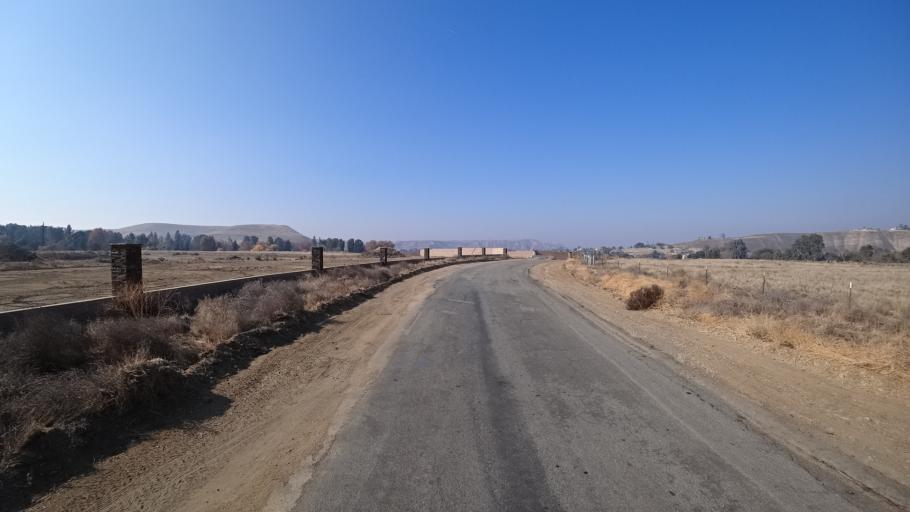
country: US
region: California
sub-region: Kern County
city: Oildale
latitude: 35.4342
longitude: -118.8698
